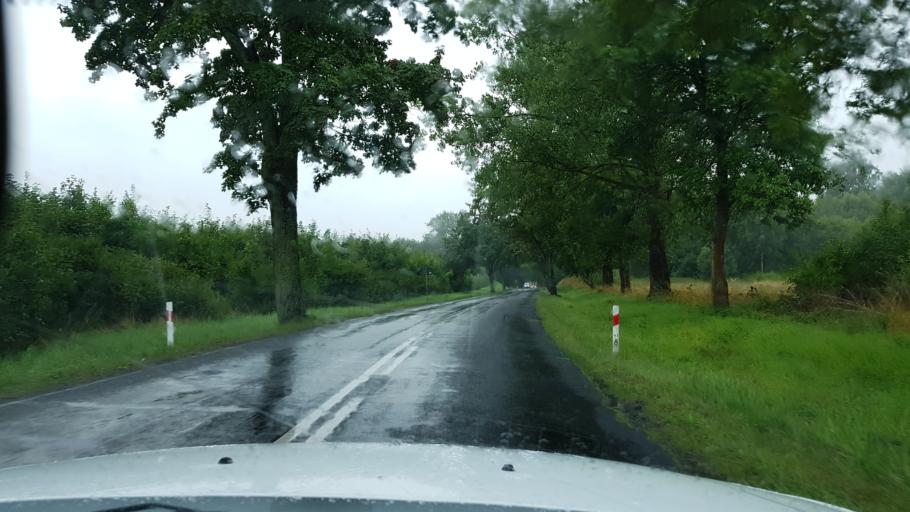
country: PL
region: West Pomeranian Voivodeship
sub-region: Powiat goleniowski
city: Nowogard
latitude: 53.5982
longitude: 15.1556
